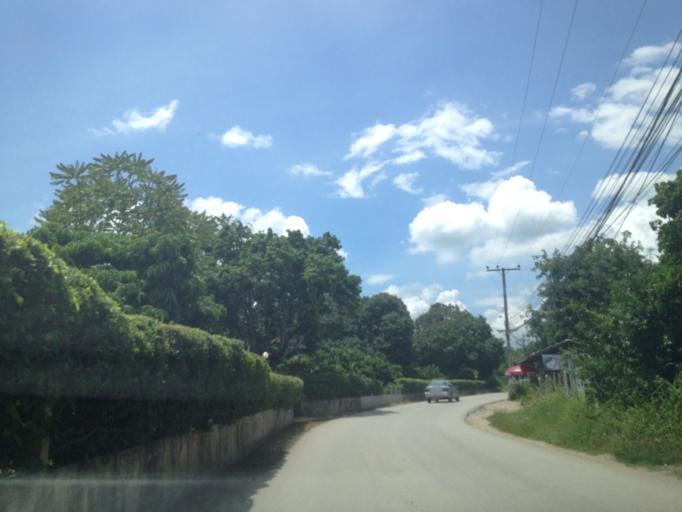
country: TH
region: Chiang Mai
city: Hang Dong
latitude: 18.6861
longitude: 98.8951
